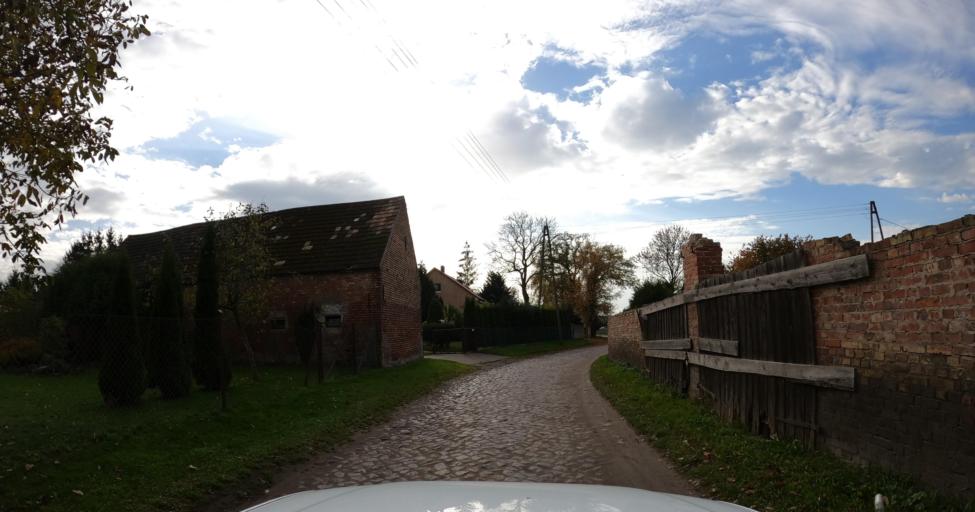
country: PL
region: West Pomeranian Voivodeship
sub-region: Powiat kamienski
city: Kamien Pomorski
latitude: 53.9744
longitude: 14.8479
